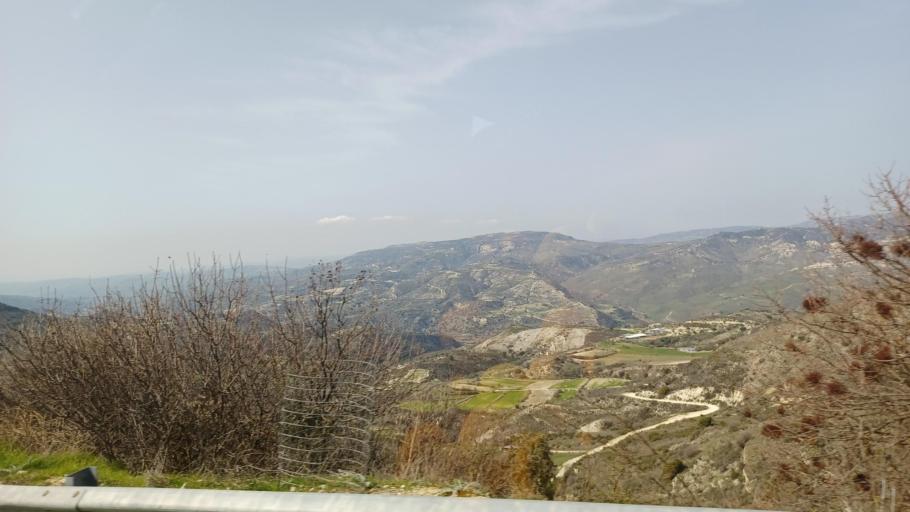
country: CY
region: Limassol
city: Pachna
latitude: 34.7977
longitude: 32.7411
